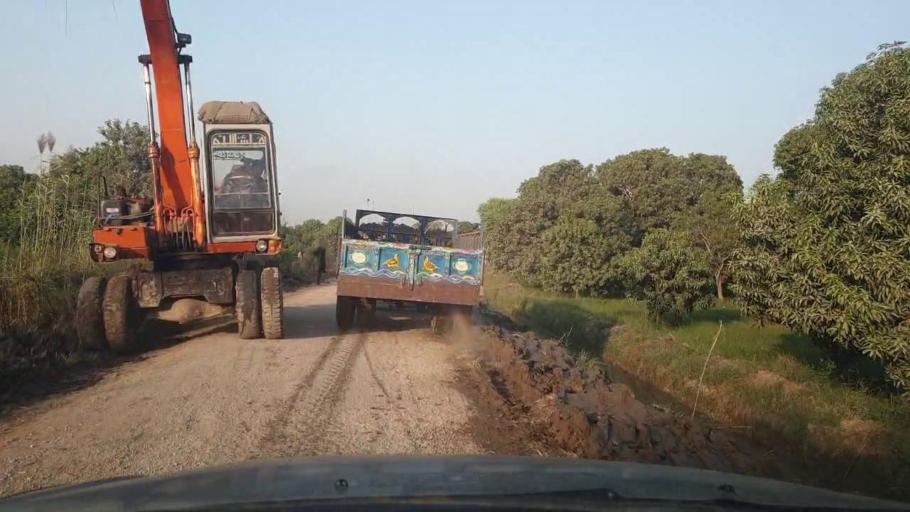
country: PK
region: Sindh
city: Tando Jam
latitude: 25.4230
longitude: 68.4937
